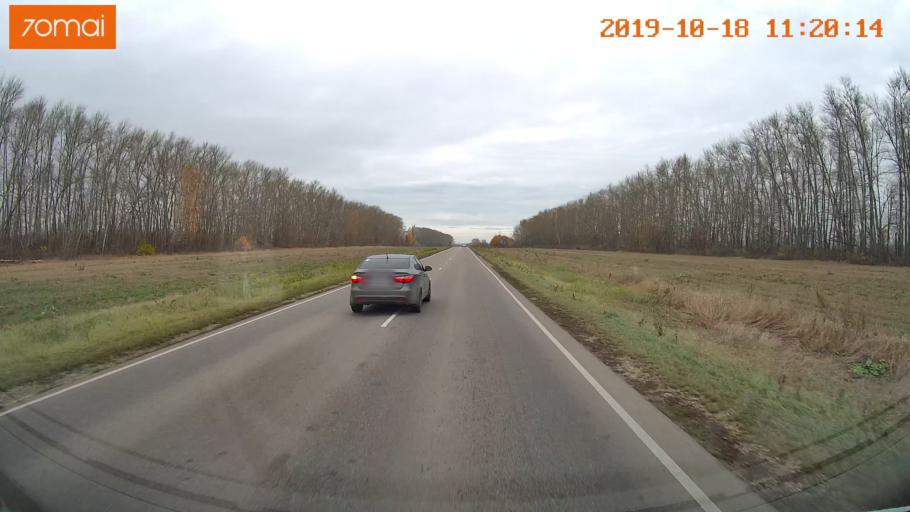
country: RU
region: Tula
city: Kimovsk
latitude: 54.0575
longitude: 38.5576
